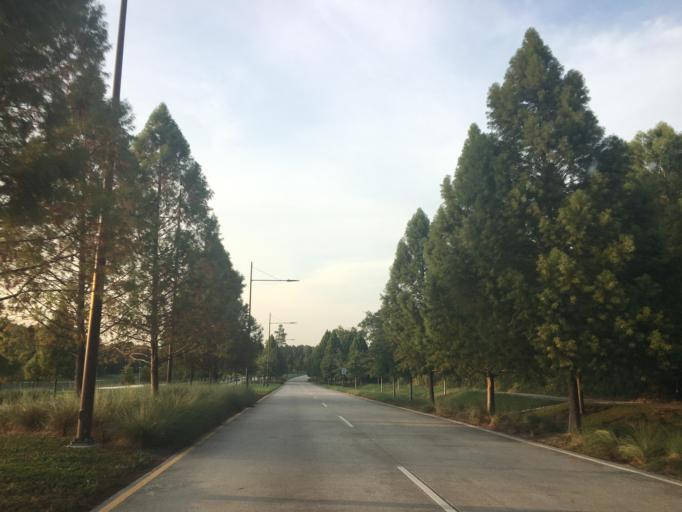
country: US
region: Texas
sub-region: Harris County
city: Spring
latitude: 30.0991
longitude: -95.4385
